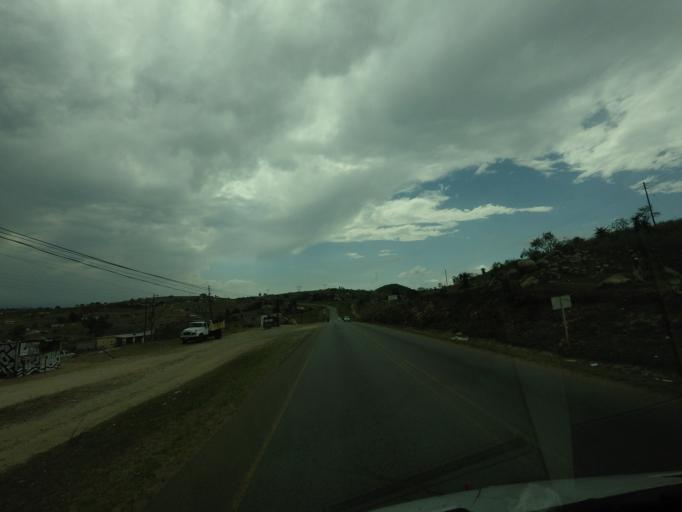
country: SZ
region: Manzini
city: Manzini
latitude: -26.5094
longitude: 31.5085
